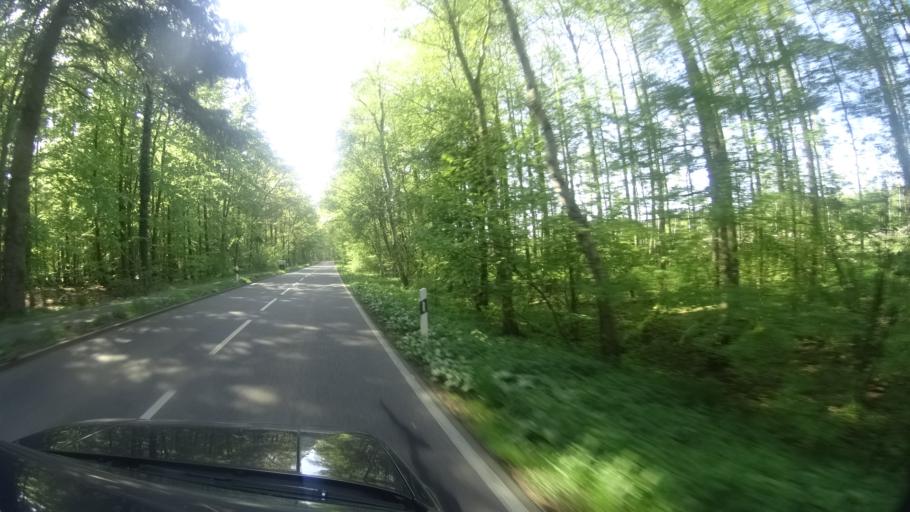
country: DE
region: Mecklenburg-Vorpommern
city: Ostseebad Dierhagen
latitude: 54.2728
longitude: 12.3325
